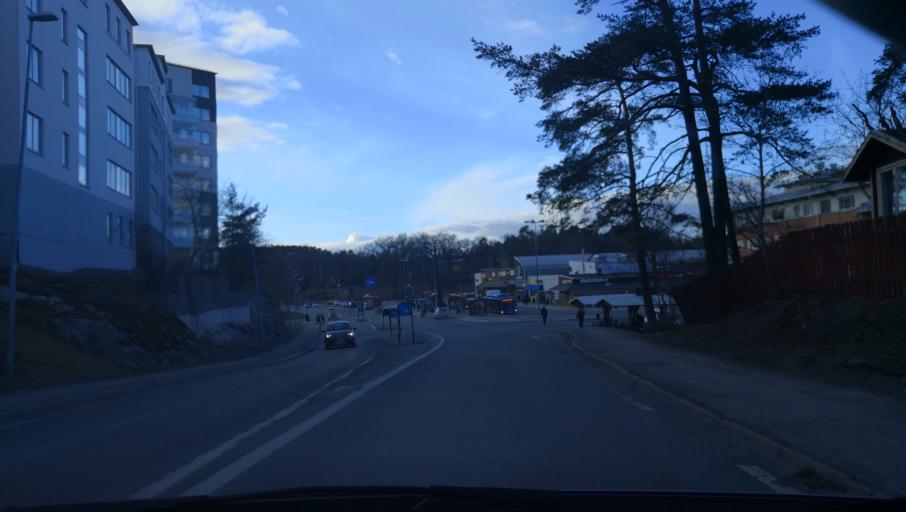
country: SE
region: Stockholm
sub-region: Varmdo Kommun
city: Gustavsberg
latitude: 59.3254
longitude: 18.3929
